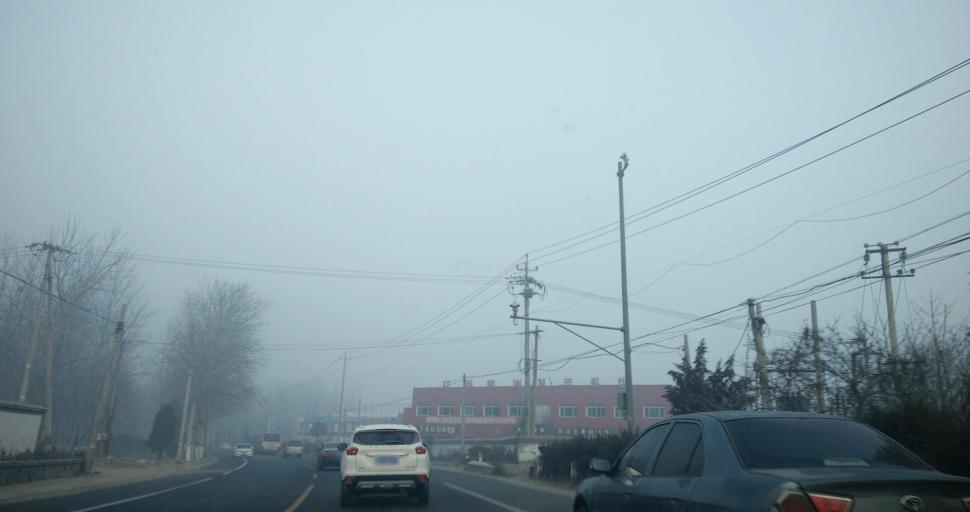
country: CN
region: Beijing
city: Yinghai
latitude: 39.7320
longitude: 116.4557
